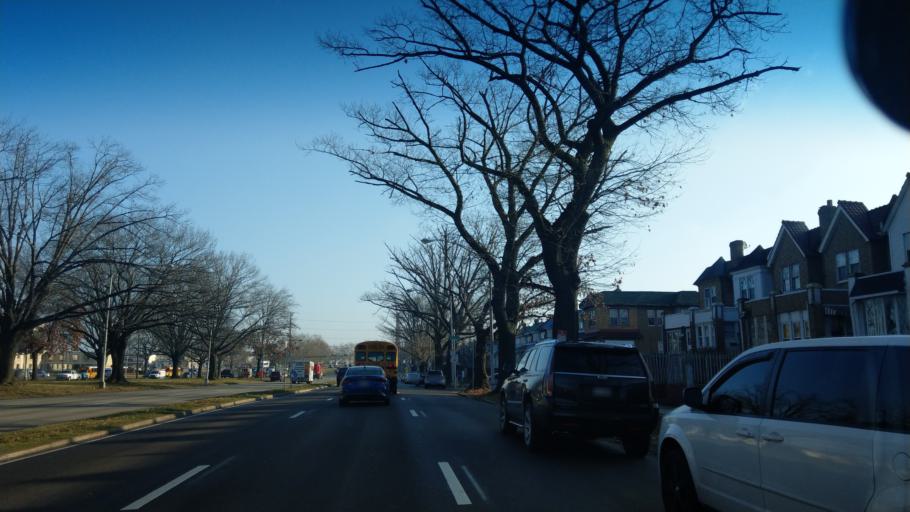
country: US
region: Pennsylvania
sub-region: Montgomery County
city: Rockledge
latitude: 40.0282
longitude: -75.1083
